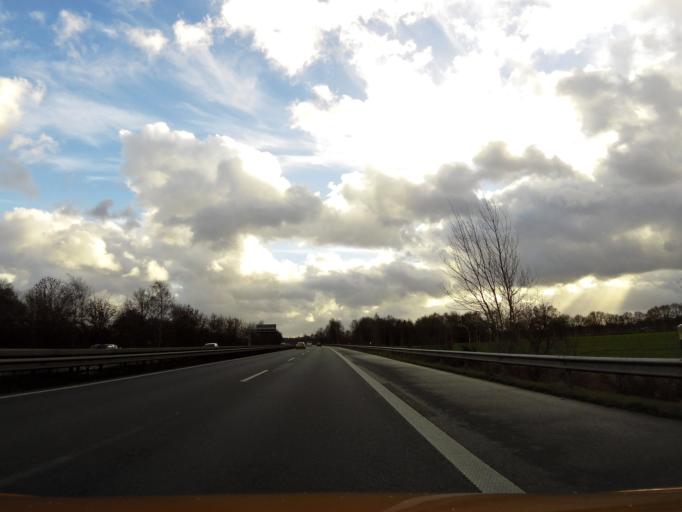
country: DE
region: Lower Saxony
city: Oldenburg
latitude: 53.0937
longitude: 8.2943
